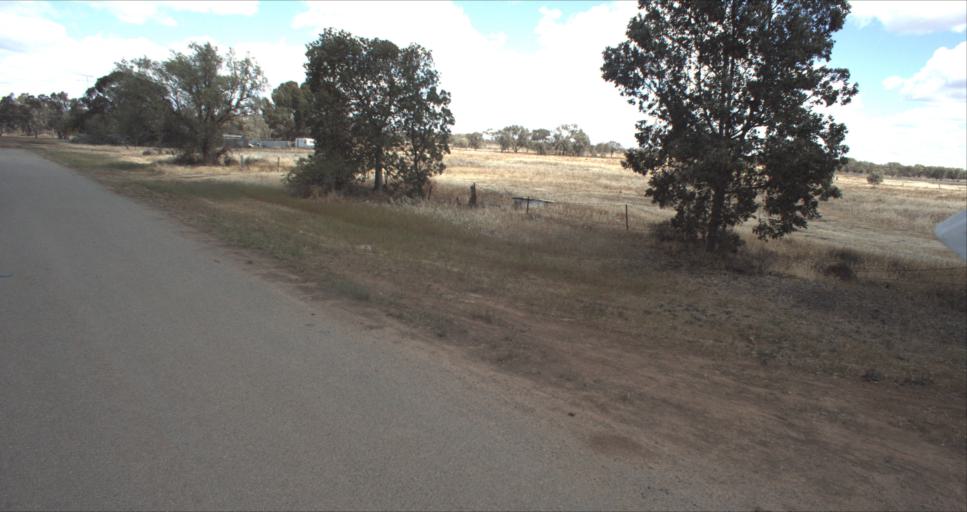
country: AU
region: New South Wales
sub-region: Murrumbidgee Shire
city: Darlington Point
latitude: -34.5182
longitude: 146.1789
